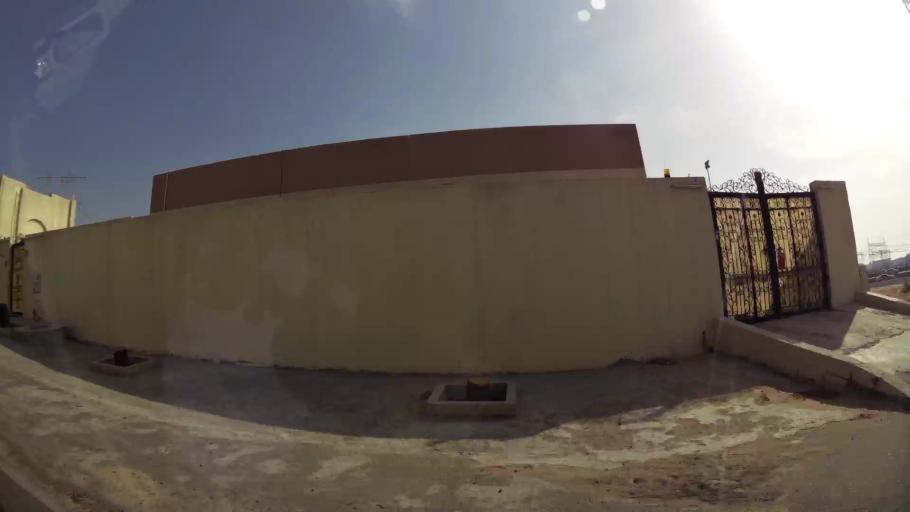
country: AE
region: Ash Shariqah
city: Sharjah
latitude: 25.2262
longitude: 55.4034
